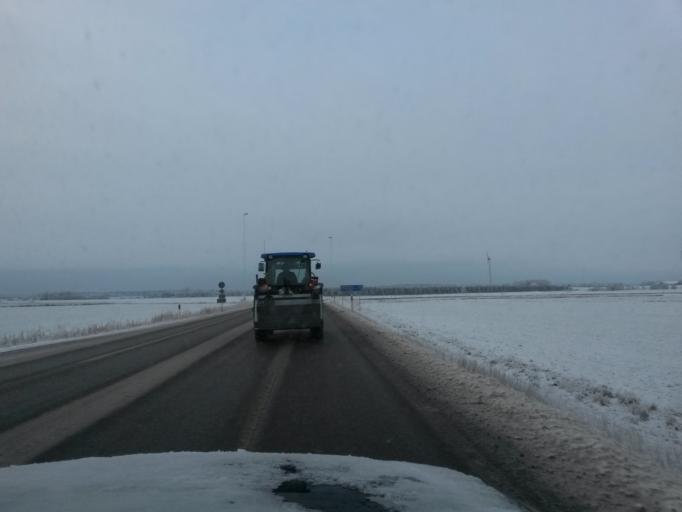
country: SE
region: Vaestra Goetaland
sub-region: Vara Kommun
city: Vara
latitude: 58.2959
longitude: 12.9546
